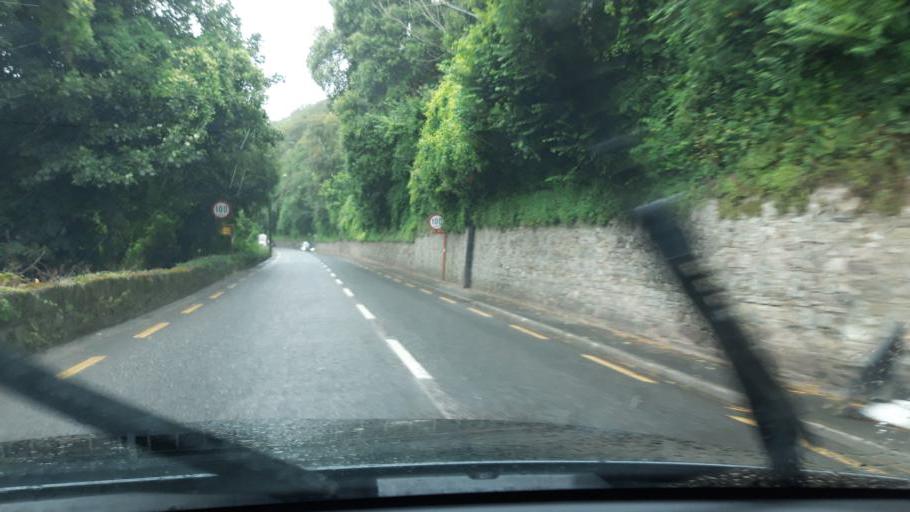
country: IE
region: Munster
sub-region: County Cork
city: Youghal
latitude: 52.1489
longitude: -7.8550
